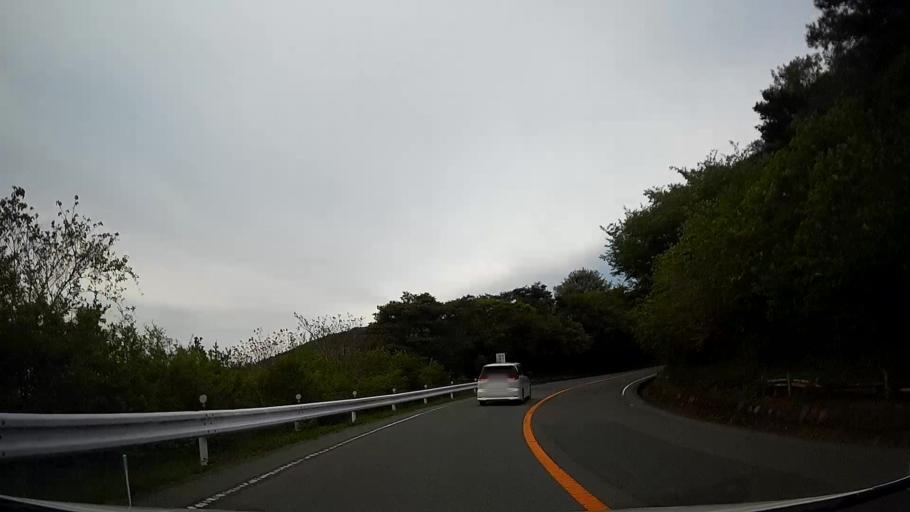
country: JP
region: Shizuoka
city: Atami
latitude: 35.0707
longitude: 139.0264
